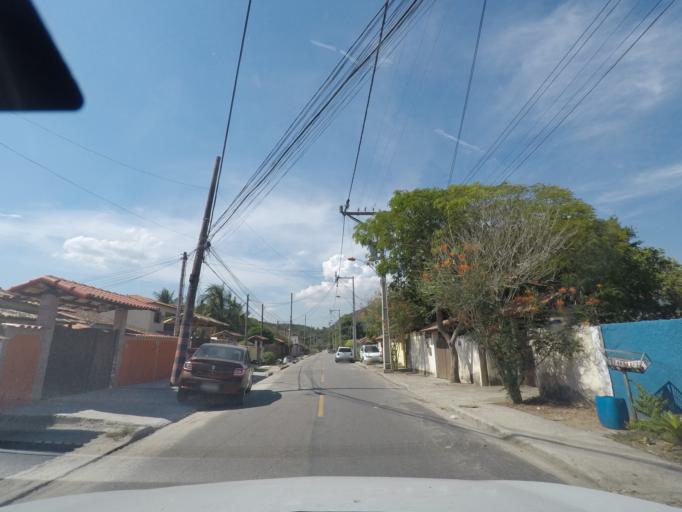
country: BR
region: Rio de Janeiro
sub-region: Marica
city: Marica
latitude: -22.9612
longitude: -42.9685
